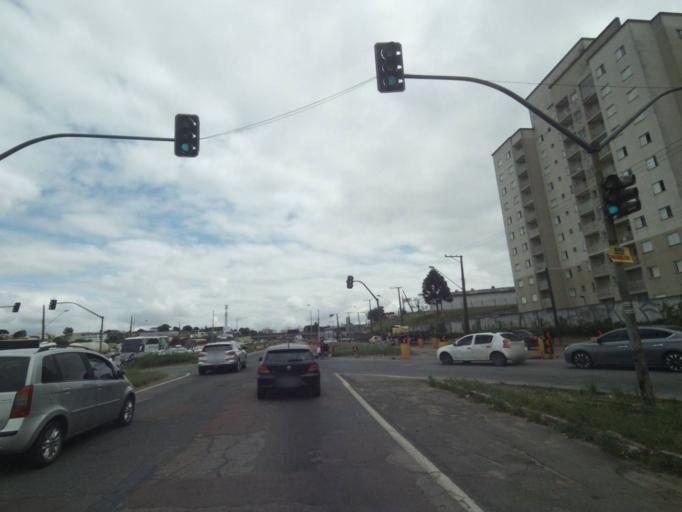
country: BR
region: Parana
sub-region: Pinhais
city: Pinhais
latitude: -25.3908
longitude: -49.2077
